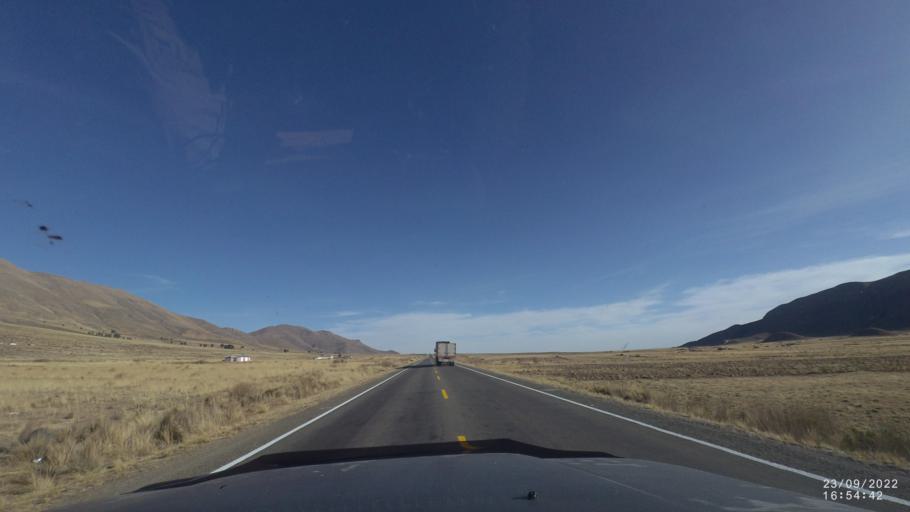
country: BO
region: Oruro
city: Poopo
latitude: -18.4681
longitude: -66.9684
